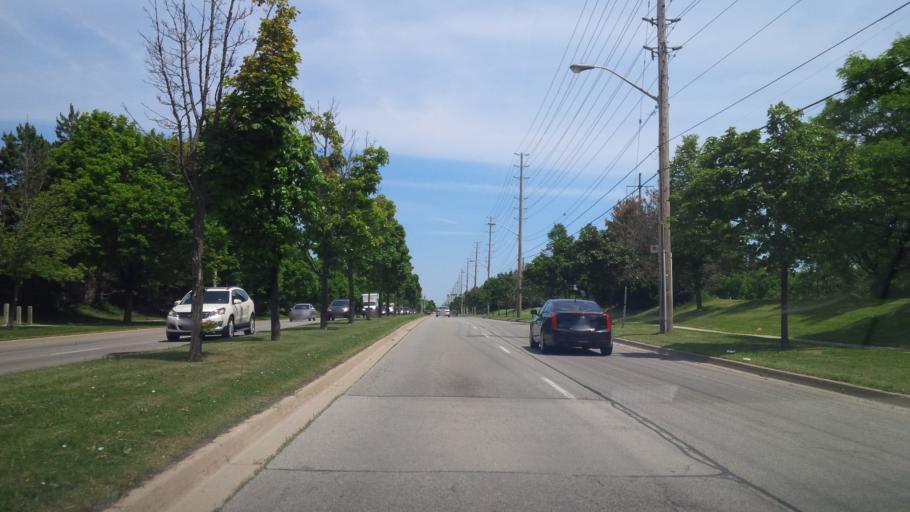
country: CA
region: Ontario
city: Burlington
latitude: 43.3707
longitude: -79.8152
